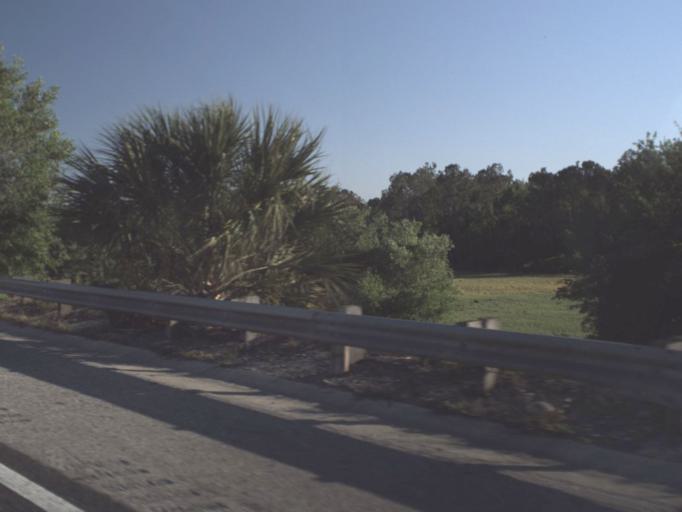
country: US
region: Florida
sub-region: Flagler County
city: Flagler Beach
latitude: 29.4968
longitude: -81.1919
